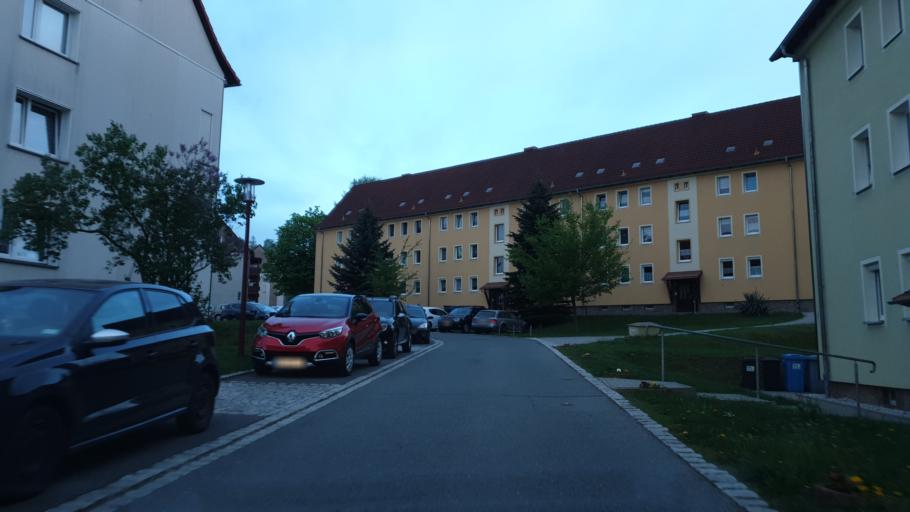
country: DE
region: Saxony
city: Hohndorf
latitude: 50.7392
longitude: 12.6804
